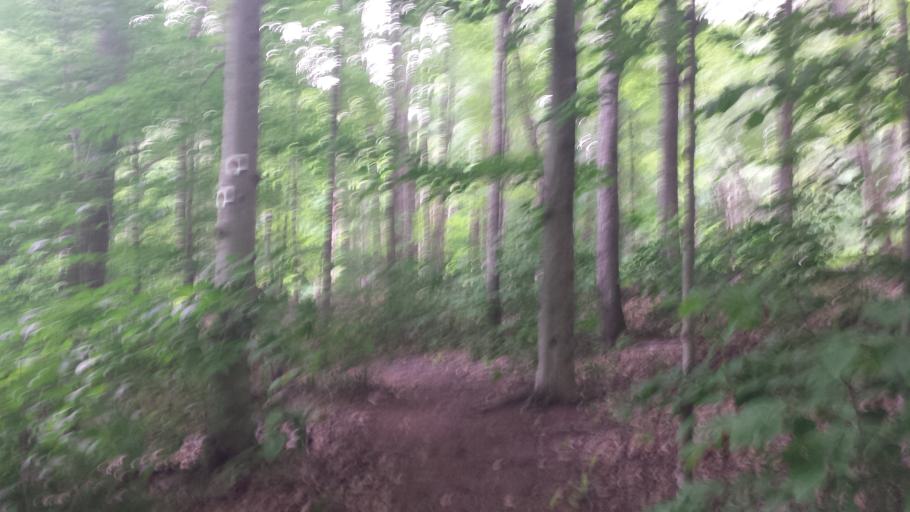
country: US
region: New York
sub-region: Westchester County
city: Pound Ridge
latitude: 41.2640
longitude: -73.5879
